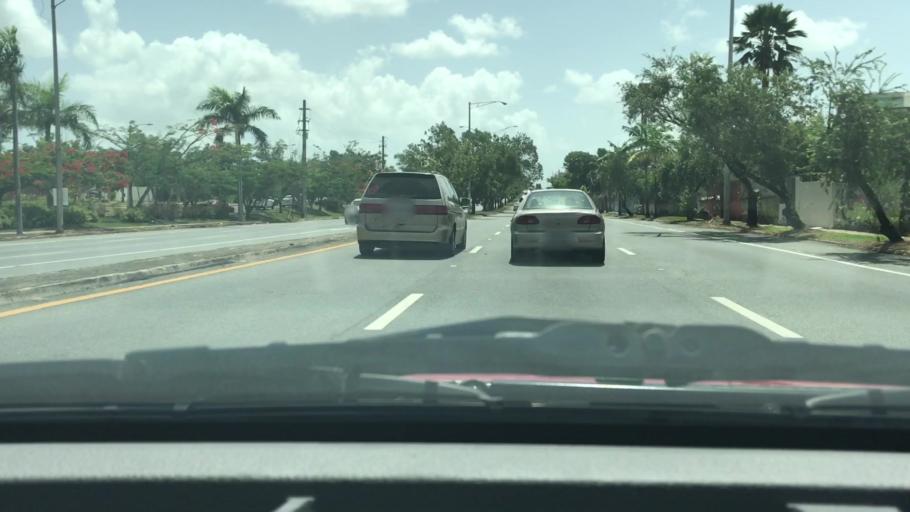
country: PR
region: Toa Alta
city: Pajaros
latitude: 18.3645
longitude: -66.1799
